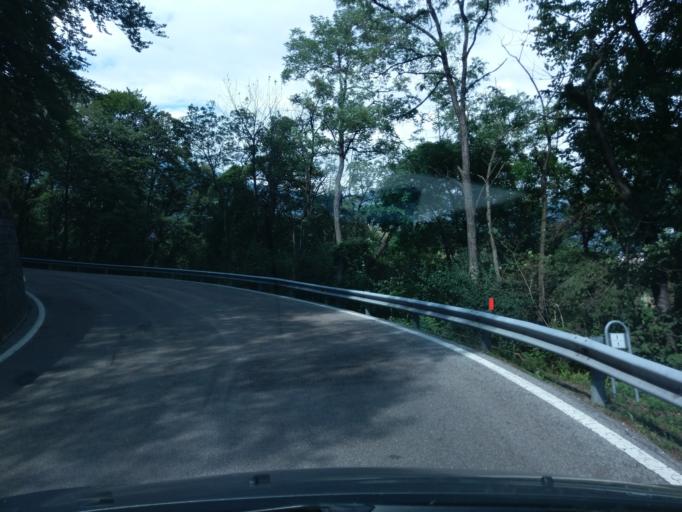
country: IT
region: Trentino-Alto Adige
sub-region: Provincia di Trento
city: Spormaggiore
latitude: 46.2364
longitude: 11.0578
